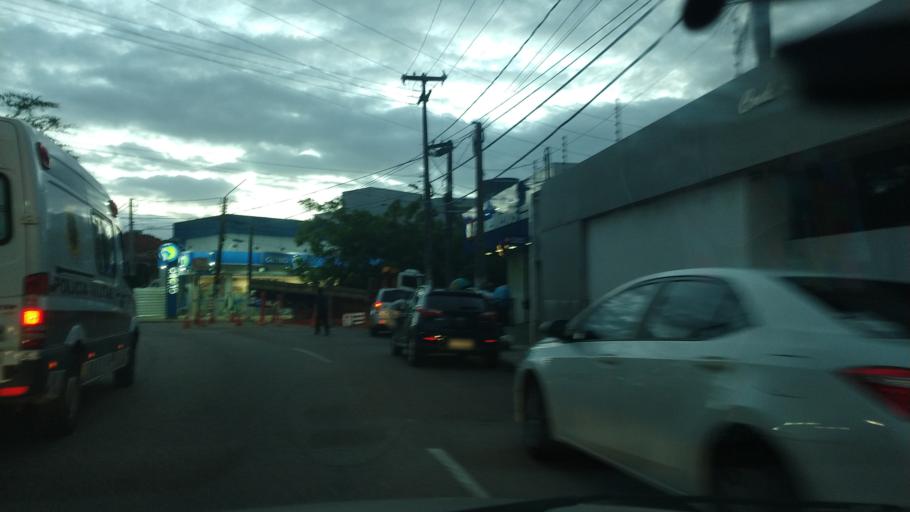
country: BR
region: Rio Grande do Norte
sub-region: Natal
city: Natal
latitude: -5.7830
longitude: -35.1994
